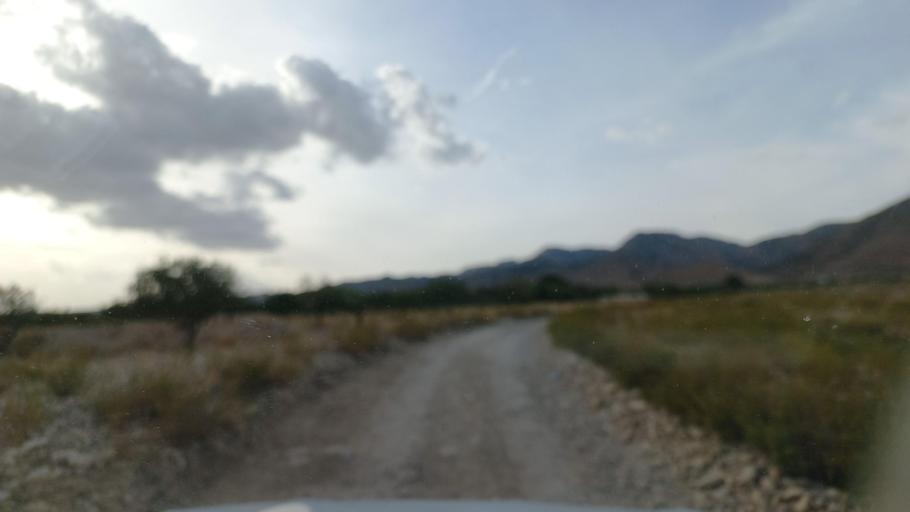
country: TN
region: Al Qasrayn
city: Sbiba
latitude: 35.4446
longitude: 9.0704
